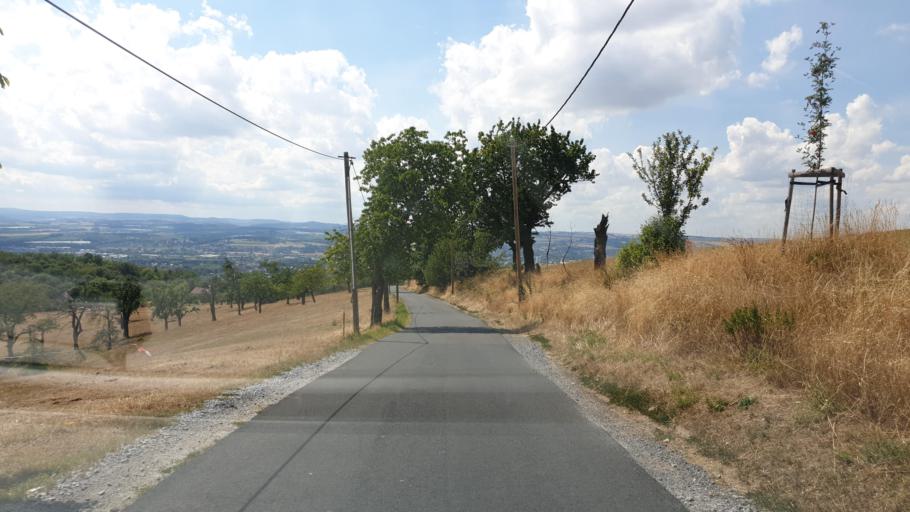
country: DE
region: Saxony
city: Heidenau
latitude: 51.0214
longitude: 13.8834
